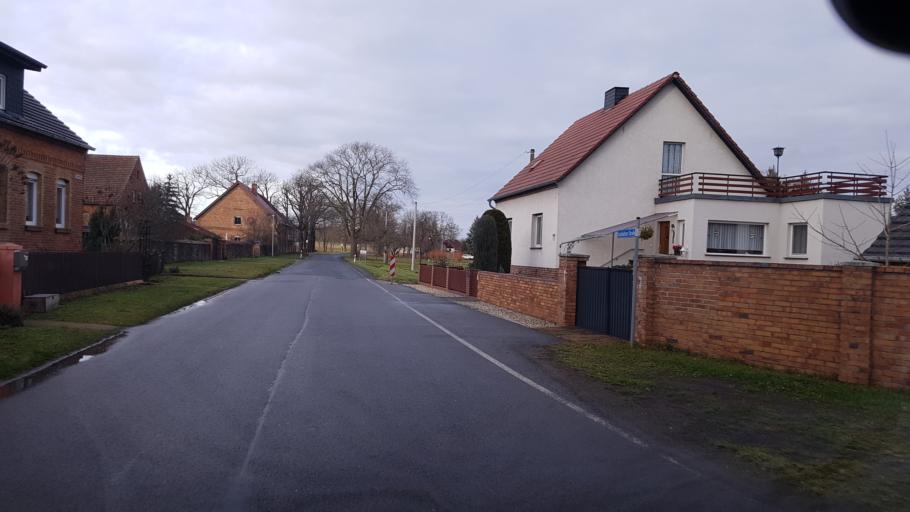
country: DE
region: Brandenburg
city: Altdobern
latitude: 51.6630
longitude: 13.9953
